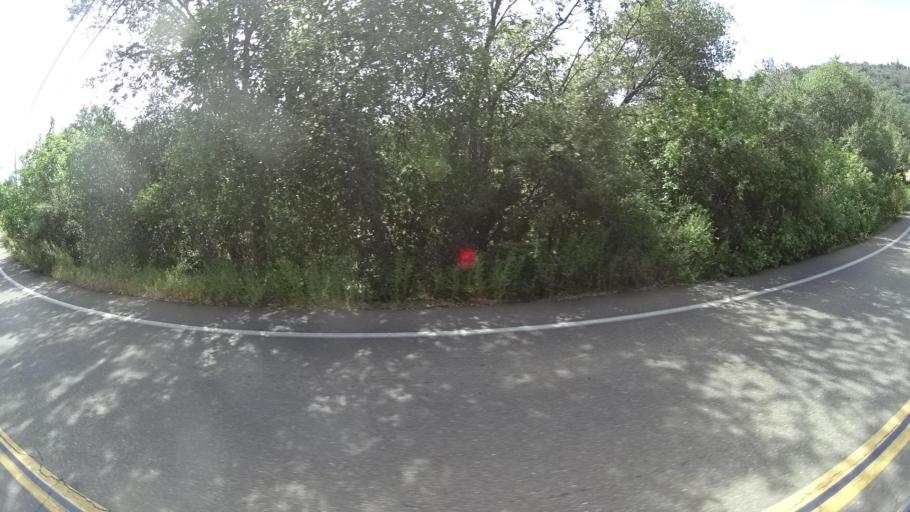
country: US
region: California
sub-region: Lake County
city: Soda Bay
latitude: 38.9716
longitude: -122.7441
